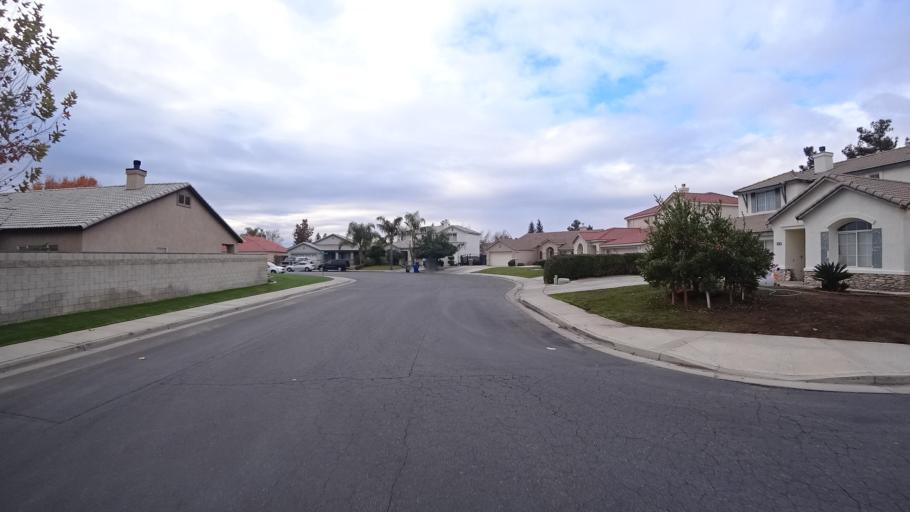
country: US
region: California
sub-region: Kern County
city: Greenfield
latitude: 35.3014
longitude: -119.0808
